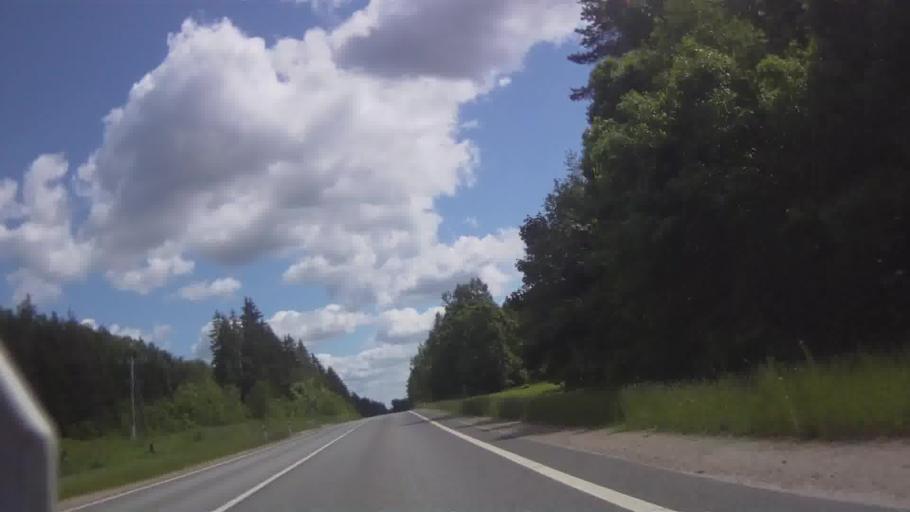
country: LV
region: Jekabpils Rajons
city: Jekabpils
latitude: 56.5327
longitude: 26.0155
